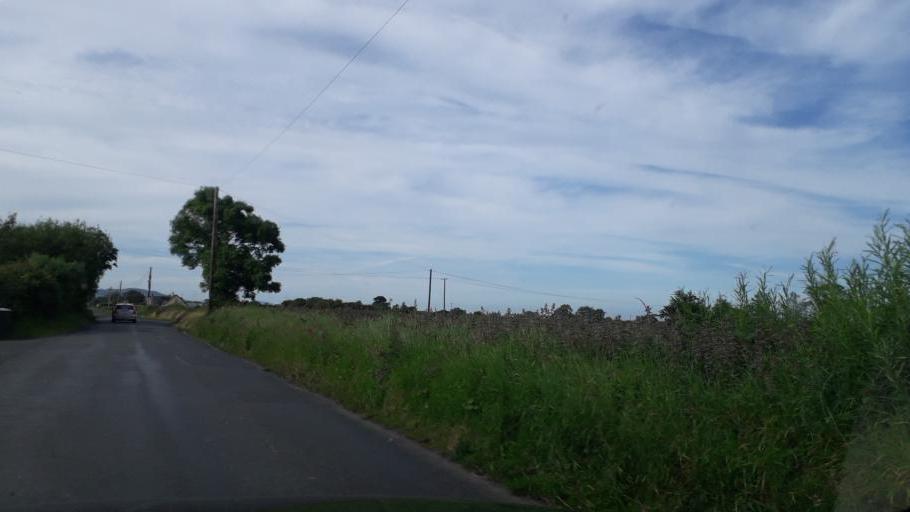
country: IE
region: Leinster
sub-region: Loch Garman
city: Courtown
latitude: 52.5875
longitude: -6.2304
